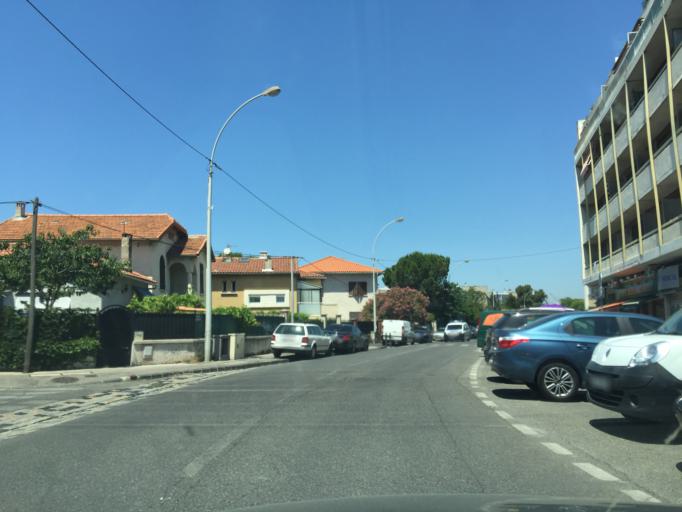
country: FR
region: Provence-Alpes-Cote d'Azur
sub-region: Departement des Bouches-du-Rhone
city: Marseille 09
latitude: 43.2511
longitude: 5.3950
